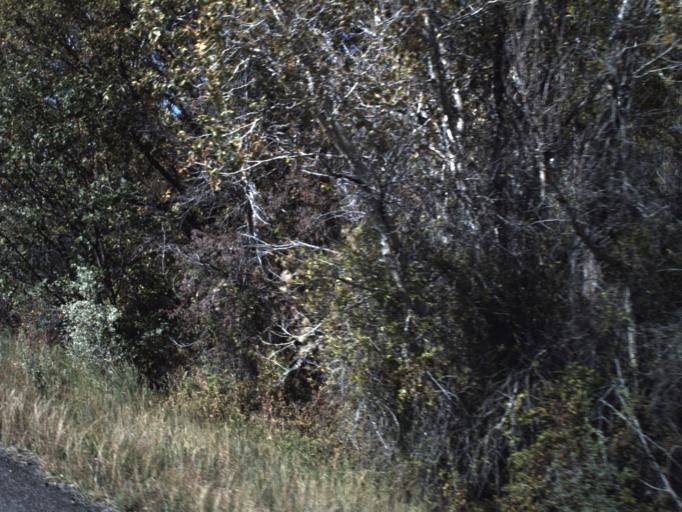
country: US
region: Utah
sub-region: Garfield County
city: Panguitch
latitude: 37.6569
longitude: -112.0907
